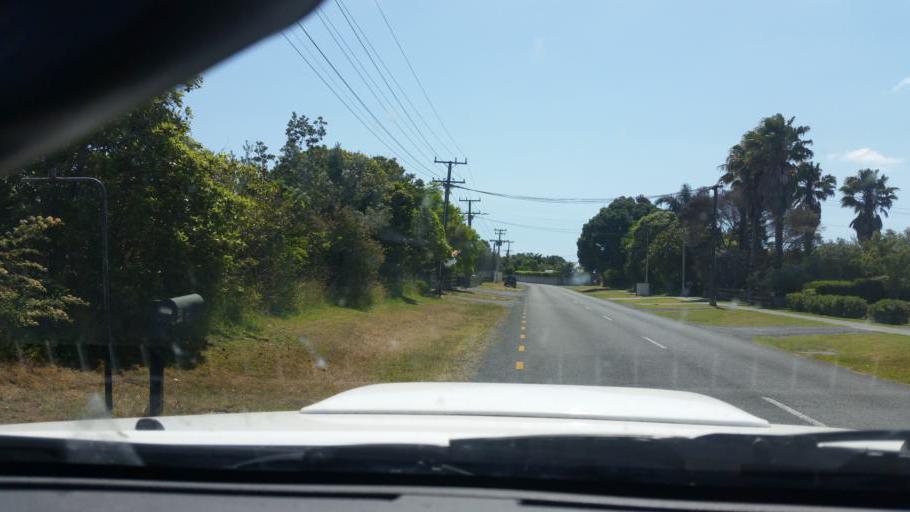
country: NZ
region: Auckland
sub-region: Auckland
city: Wellsford
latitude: -36.1254
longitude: 174.5770
